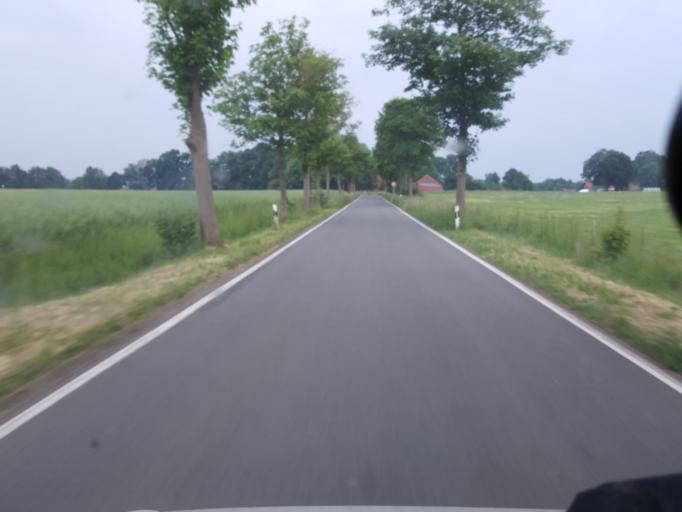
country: DE
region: North Rhine-Westphalia
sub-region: Regierungsbezirk Detmold
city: Minden
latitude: 52.3612
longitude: 8.8574
